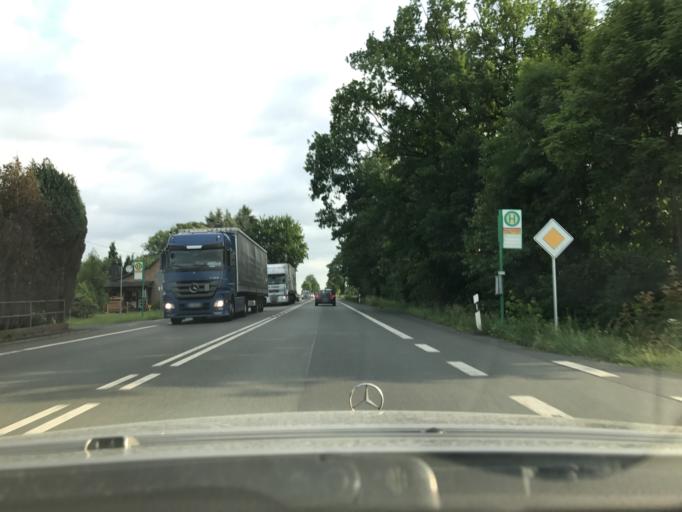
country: DE
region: North Rhine-Westphalia
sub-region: Regierungsbezirk Arnsberg
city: Werl
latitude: 51.6054
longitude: 7.8532
